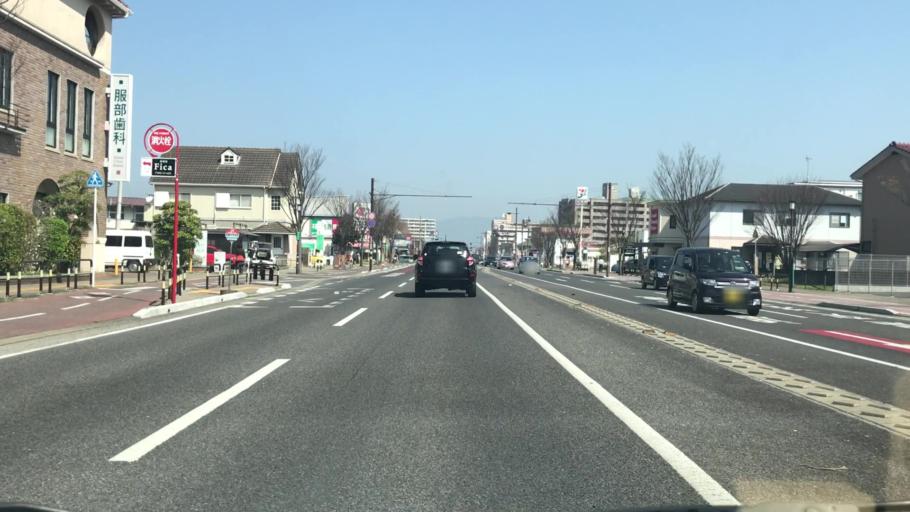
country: JP
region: Saga Prefecture
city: Saga-shi
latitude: 33.2558
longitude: 130.2929
